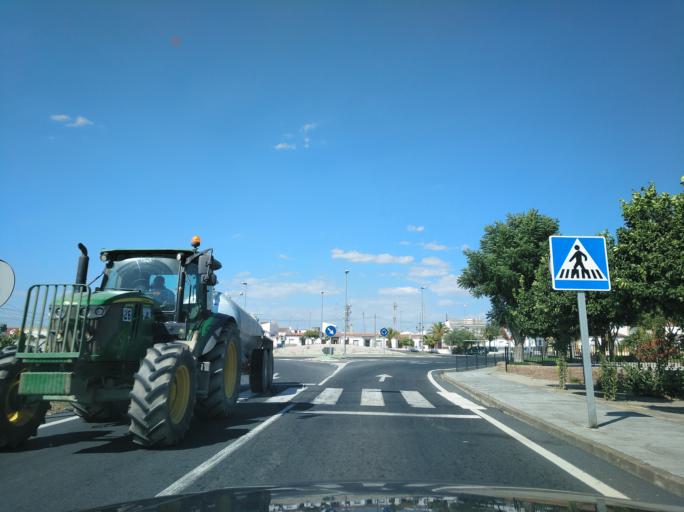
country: ES
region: Andalusia
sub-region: Provincia de Huelva
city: Alosno
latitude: 37.5488
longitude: -7.1203
